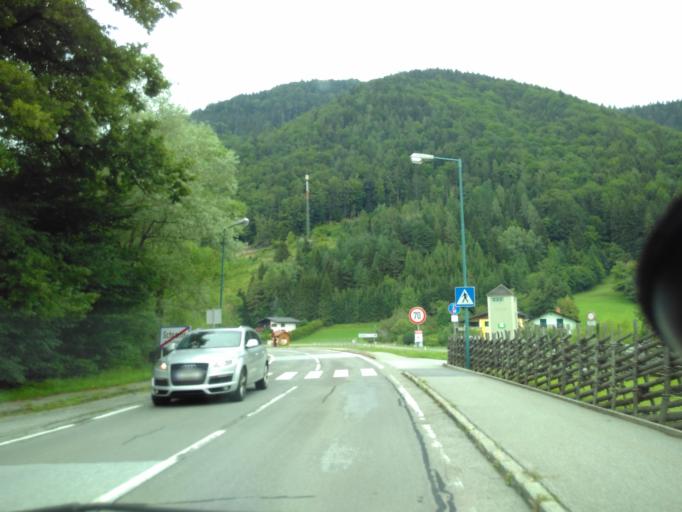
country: AT
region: Styria
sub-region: Politischer Bezirk Graz-Umgebung
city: Schrems bei Frohnleiten
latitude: 47.2805
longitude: 15.3609
